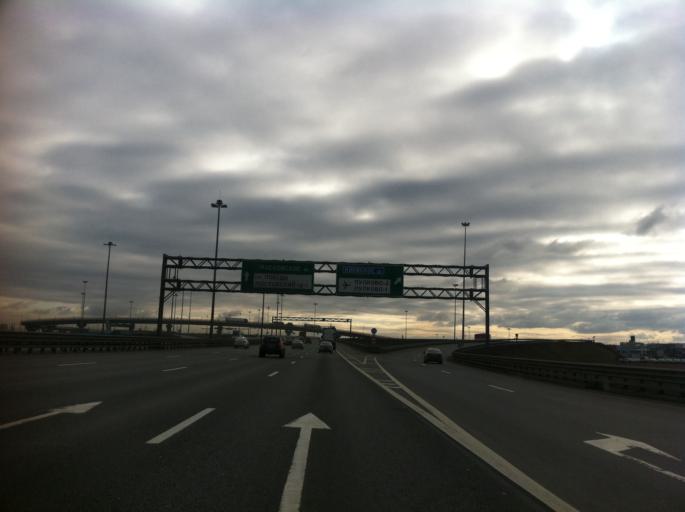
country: RU
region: St.-Petersburg
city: Kupchino
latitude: 59.8141
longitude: 30.3157
